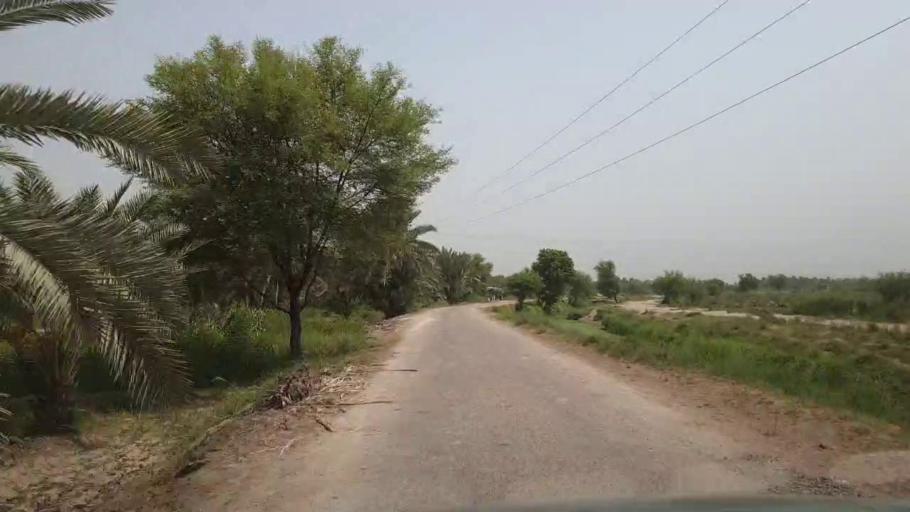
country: PK
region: Sindh
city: Gambat
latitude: 27.4213
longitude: 68.5542
